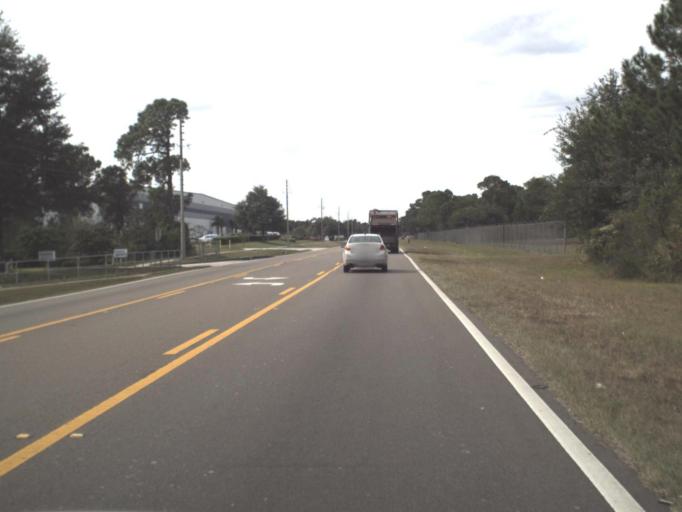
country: US
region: Florida
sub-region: Orange County
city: Taft
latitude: 28.4363
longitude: -81.3528
